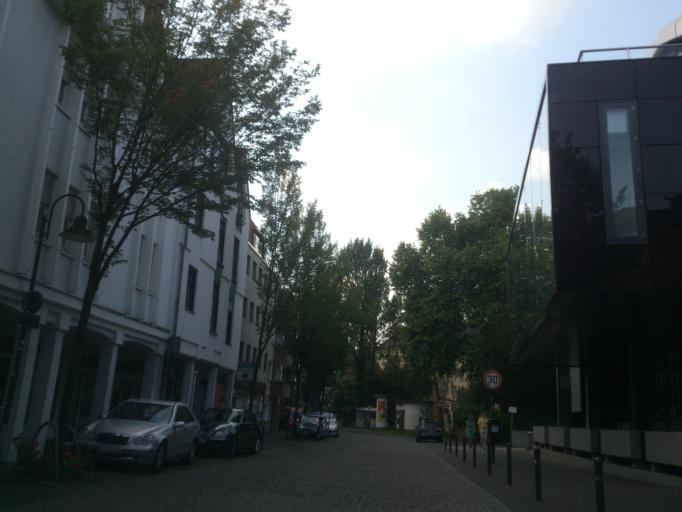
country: DE
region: North Rhine-Westphalia
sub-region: Regierungsbezirk Detmold
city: Paderborn
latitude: 51.7213
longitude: 8.7545
